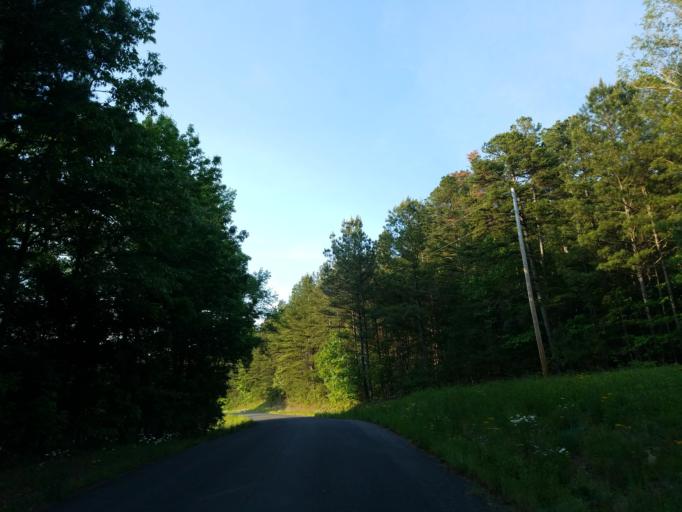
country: US
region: Georgia
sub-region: Whitfield County
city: Dalton
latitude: 34.6541
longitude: -85.0822
